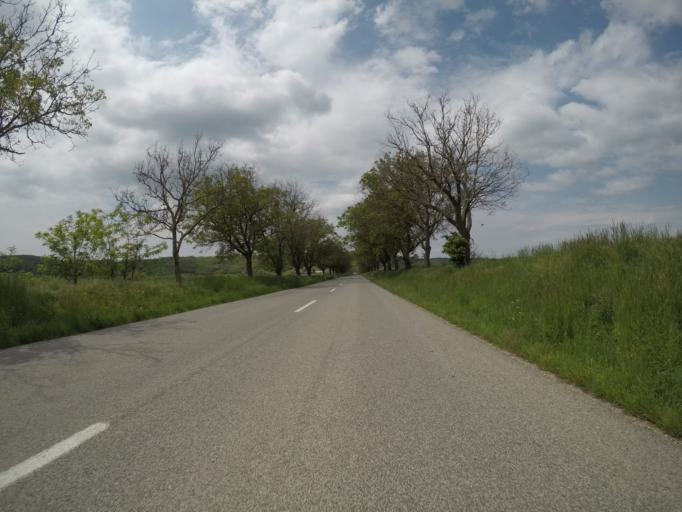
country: SK
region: Banskobystricky
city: Dudince
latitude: 48.0803
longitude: 18.8129
